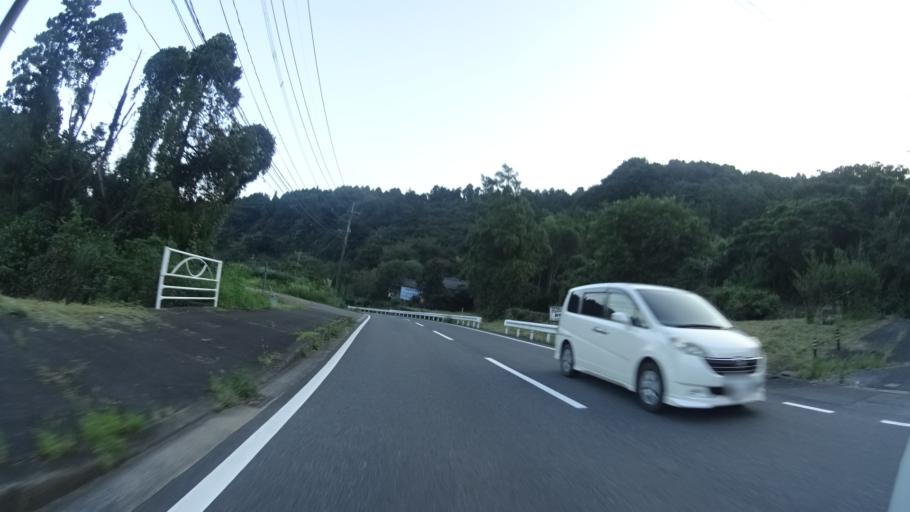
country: JP
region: Oita
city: Beppu
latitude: 33.3263
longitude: 131.4498
